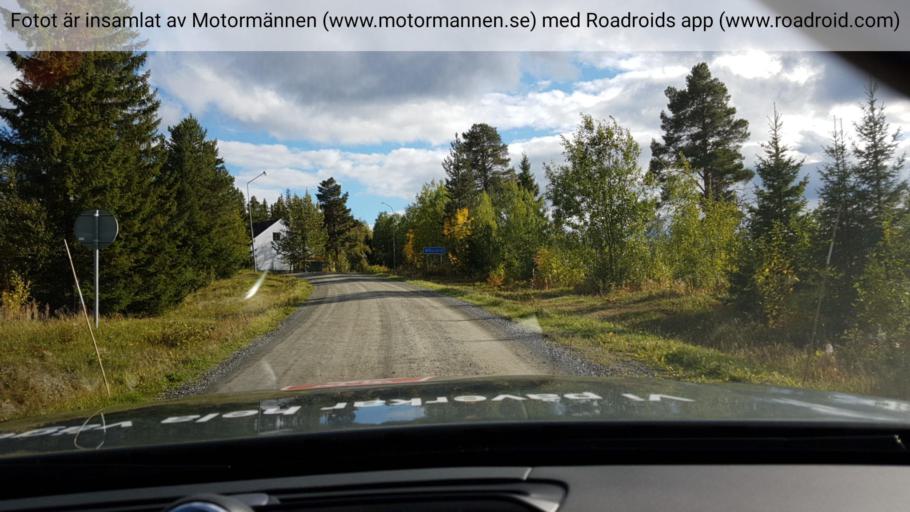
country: SE
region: Jaemtland
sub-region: Are Kommun
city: Jarpen
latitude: 63.2343
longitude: 13.6763
